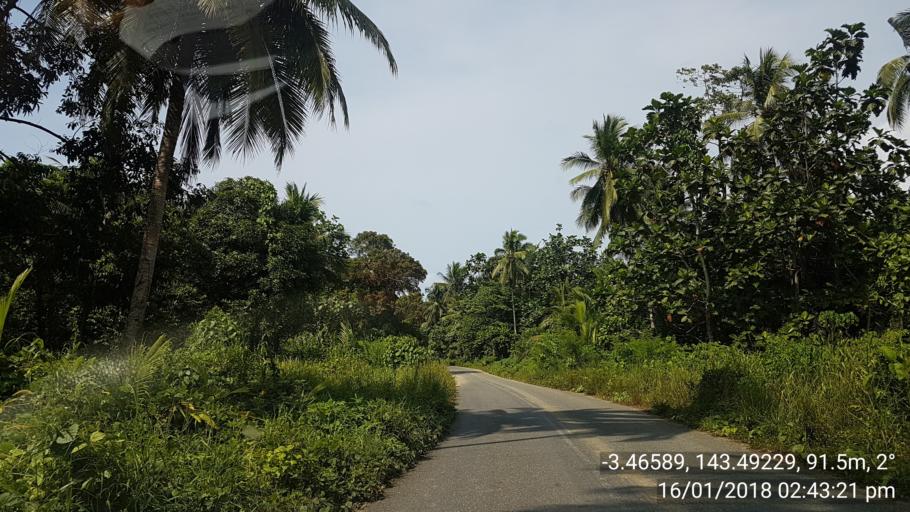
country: PG
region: East Sepik
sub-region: Wewak
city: Wewak
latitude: -3.4658
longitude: 143.4922
